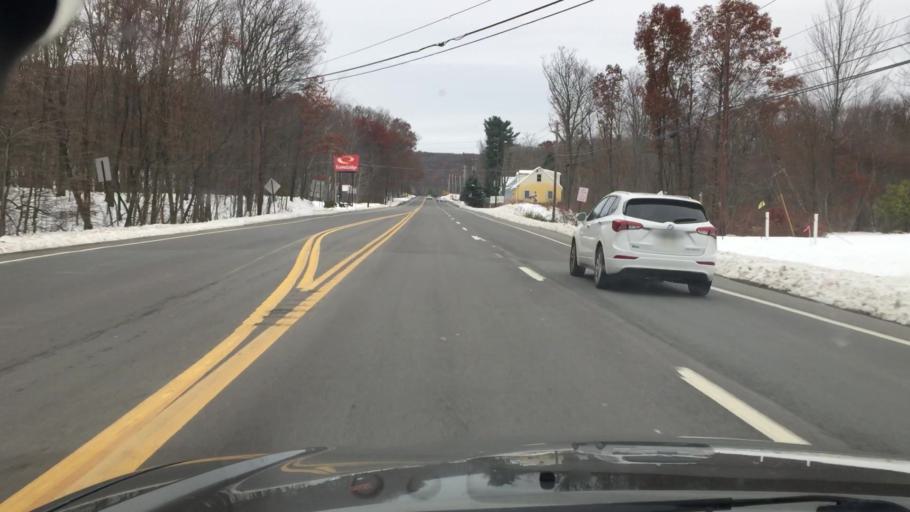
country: US
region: Pennsylvania
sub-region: Luzerne County
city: Freeland
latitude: 41.0563
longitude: -75.9610
